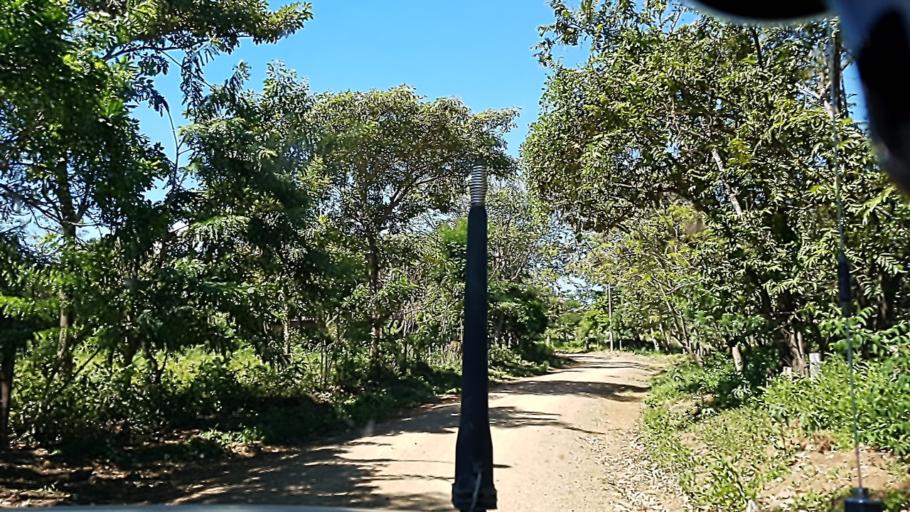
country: NI
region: Carazo
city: Santa Teresa
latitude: 11.7126
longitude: -86.1744
